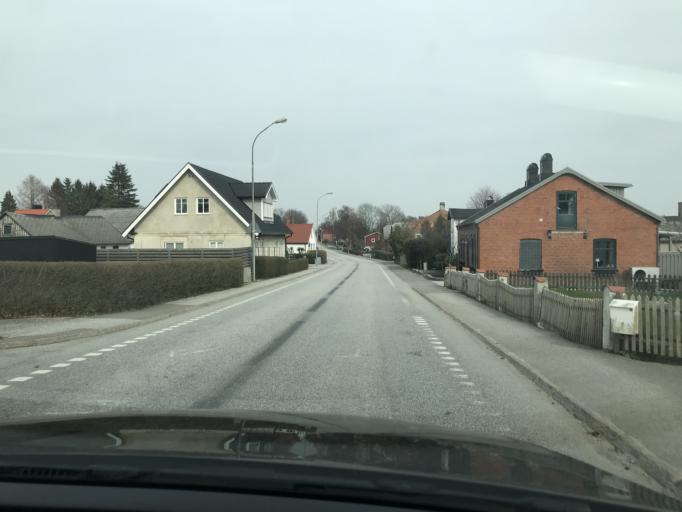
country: SE
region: Skane
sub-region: Skurups Kommun
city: Skivarp
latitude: 55.4232
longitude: 13.5740
